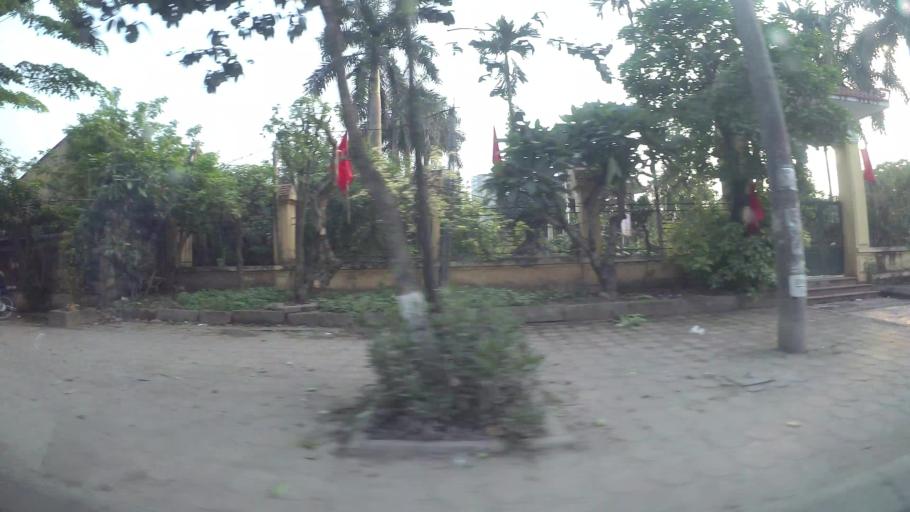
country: VN
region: Ha Noi
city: Thanh Xuan
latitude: 20.9782
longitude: 105.8230
